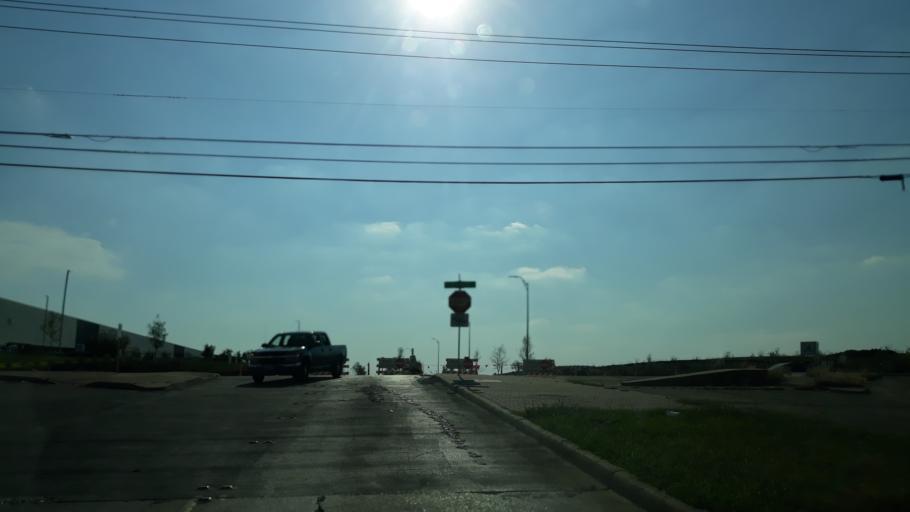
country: US
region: Texas
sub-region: Tarrant County
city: Euless
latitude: 32.8454
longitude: -97.0214
